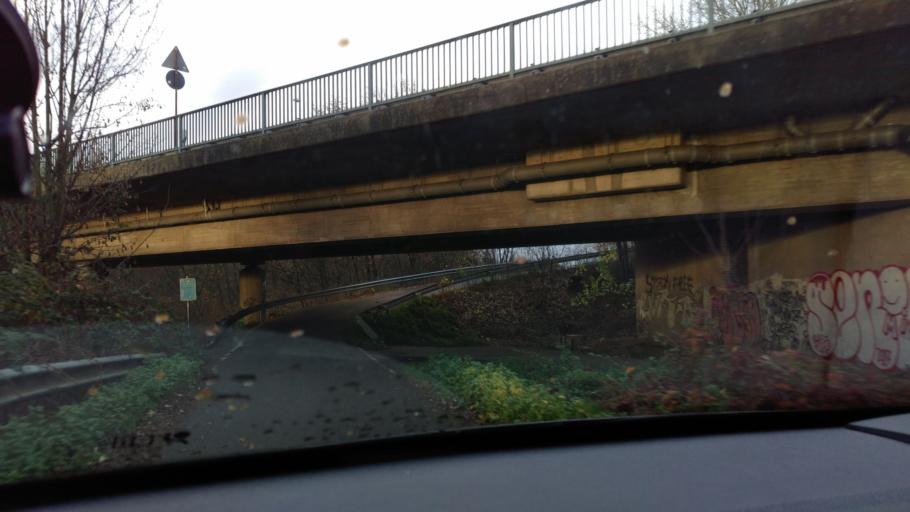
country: DE
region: North Rhine-Westphalia
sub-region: Regierungsbezirk Koln
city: Bonn
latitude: 50.7633
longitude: 7.1111
